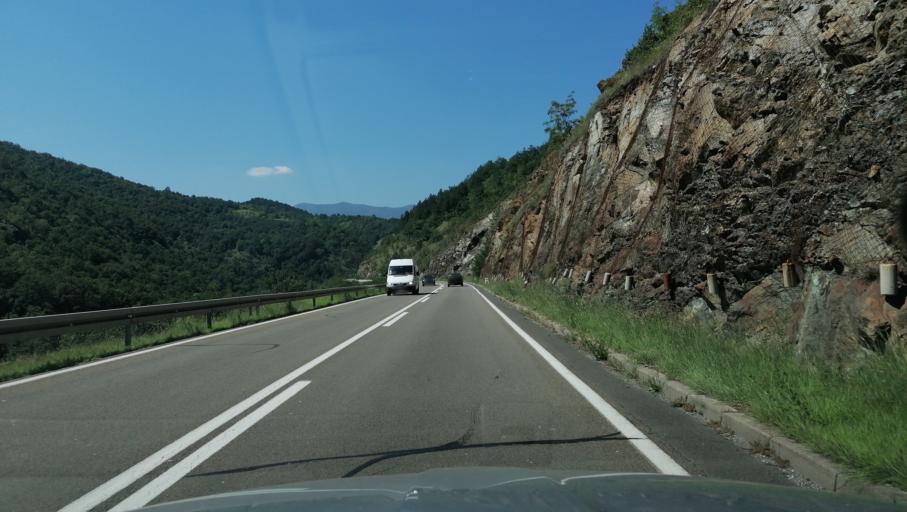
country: RS
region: Central Serbia
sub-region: Raski Okrug
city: Kraljevo
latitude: 43.6609
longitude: 20.5907
